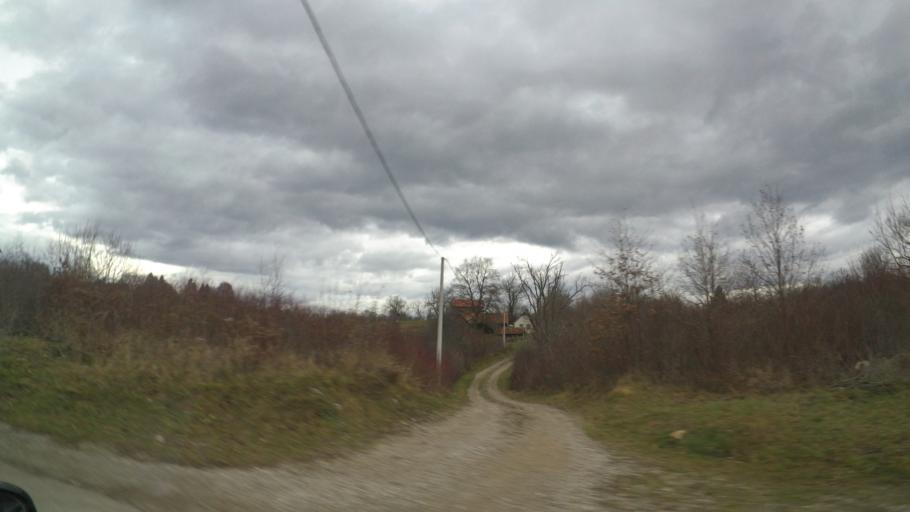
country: HR
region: Karlovacka
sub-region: Grad Karlovac
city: Karlovac
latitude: 45.3735
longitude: 15.5519
